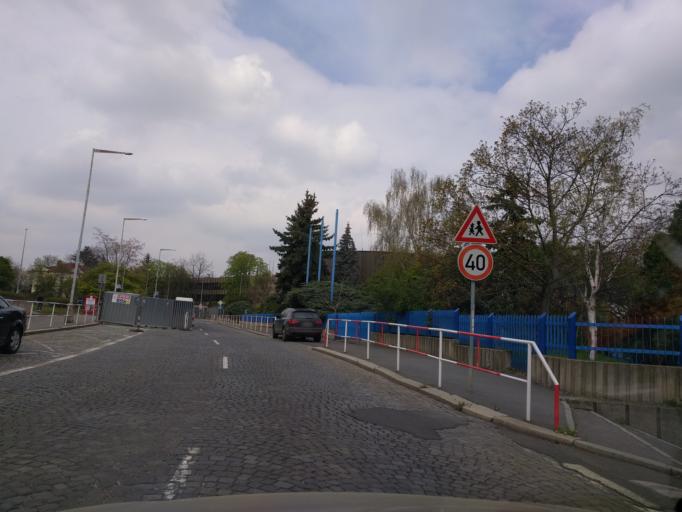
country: CZ
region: Praha
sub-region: Praha 1
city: Mala Strana
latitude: 50.1045
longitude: 14.4072
